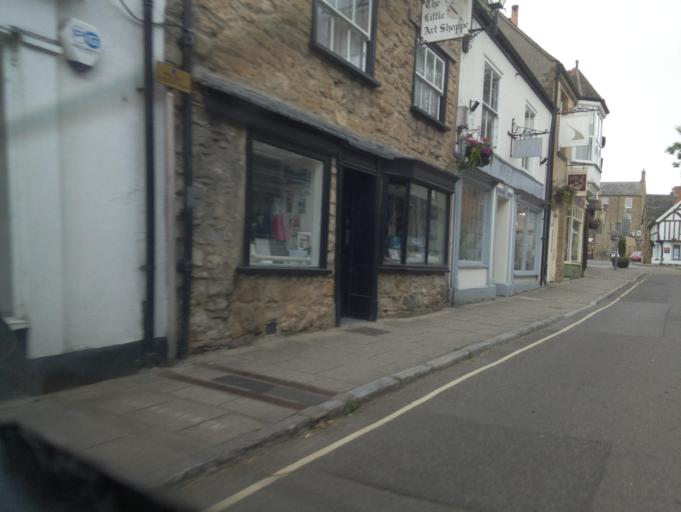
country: GB
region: England
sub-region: Dorset
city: Sherborne
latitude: 50.9495
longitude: -2.5167
